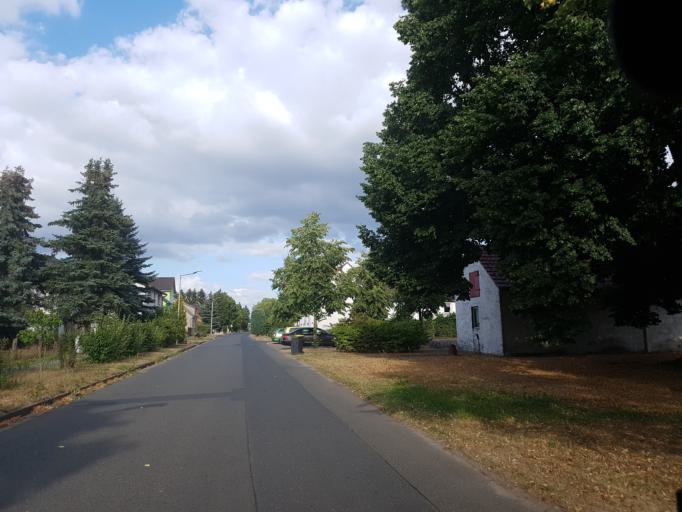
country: DE
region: Brandenburg
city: Herzberg
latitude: 51.7608
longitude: 13.2547
